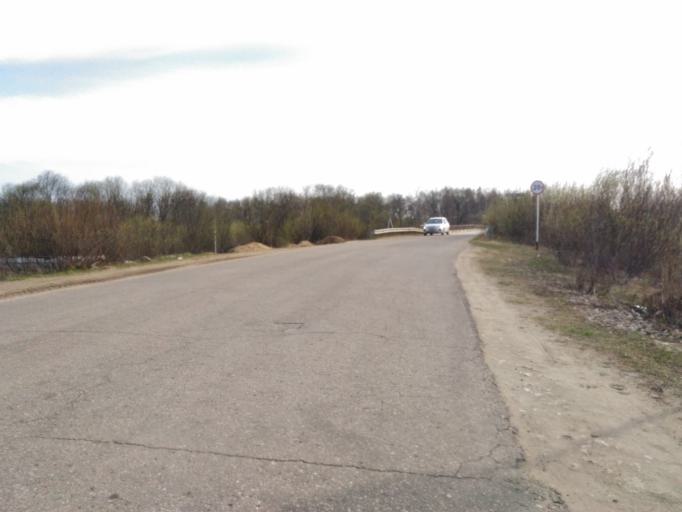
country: RU
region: Vladimir
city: Petushki
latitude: 55.9053
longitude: 39.4695
